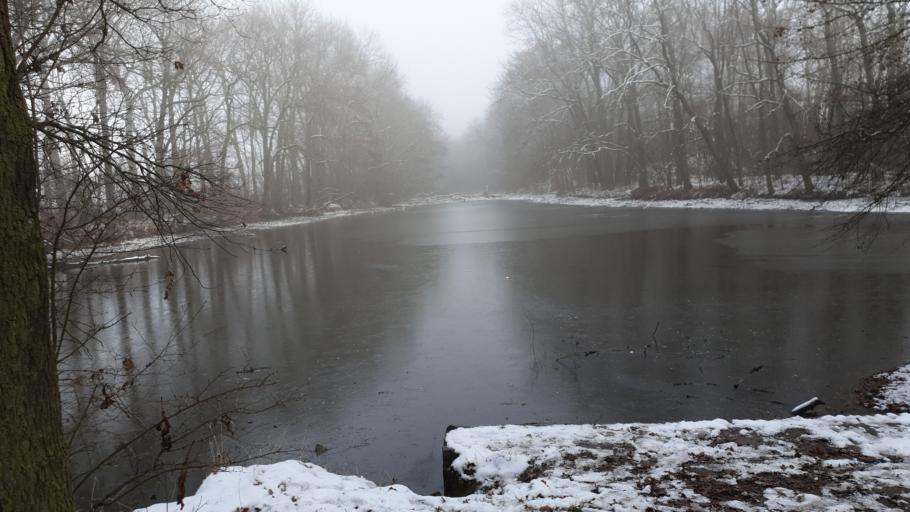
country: DE
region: Saxony
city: Taucha
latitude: 51.3987
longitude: 12.4903
